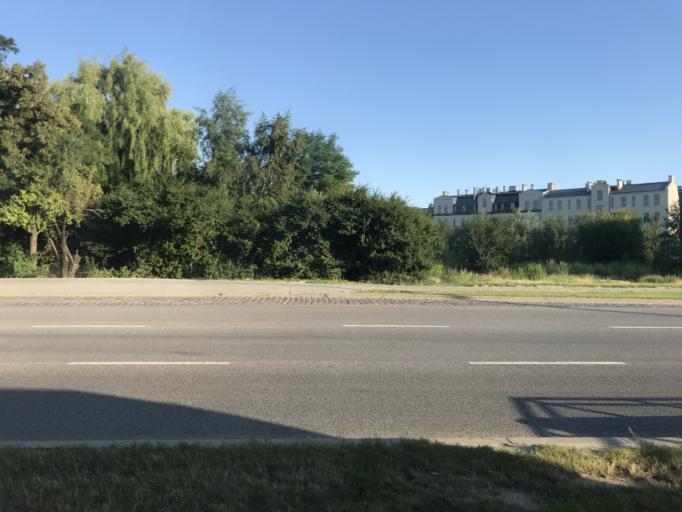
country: PL
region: Pomeranian Voivodeship
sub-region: Gdansk
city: Gdansk
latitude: 54.3446
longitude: 18.6648
